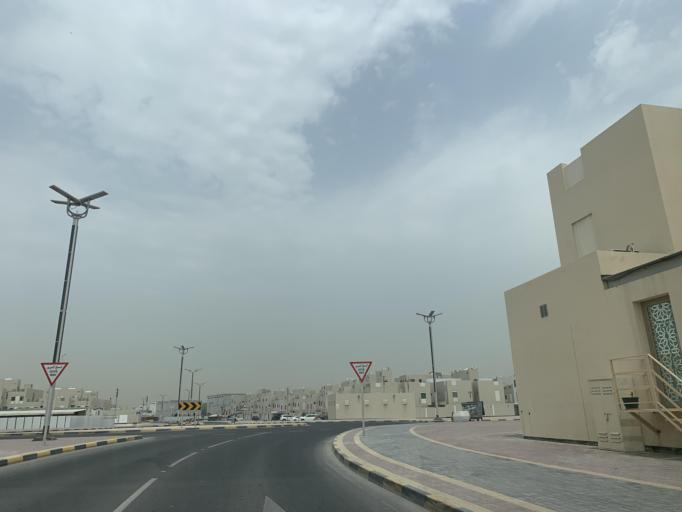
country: BH
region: Northern
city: Madinat `Isa
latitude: 26.1765
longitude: 50.5174
